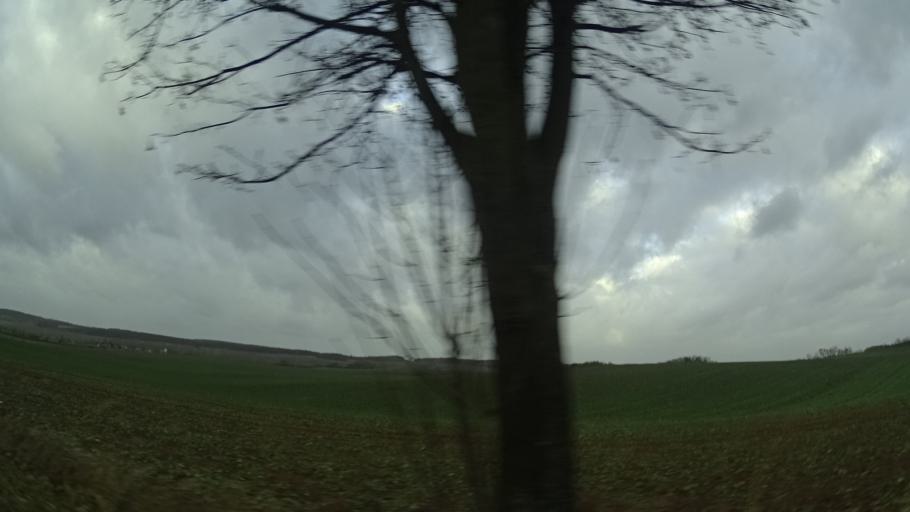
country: DE
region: Thuringia
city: Lemnitz
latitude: 50.7270
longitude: 11.8280
